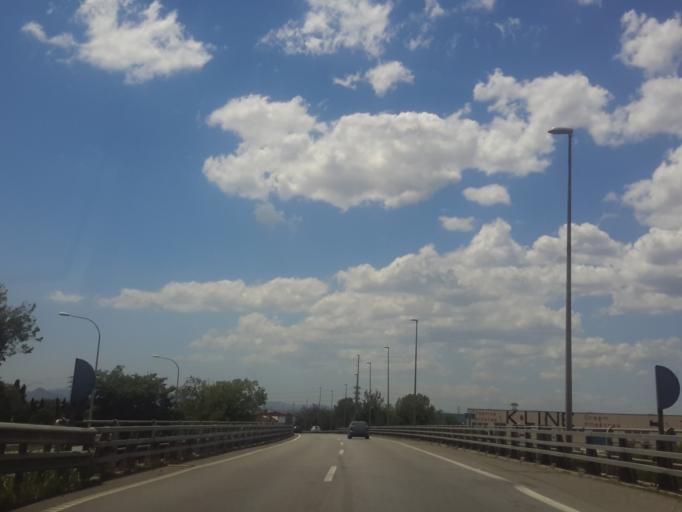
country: ES
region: Catalonia
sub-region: Provincia de Barcelona
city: Montmelo
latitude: 41.5564
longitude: 2.2411
